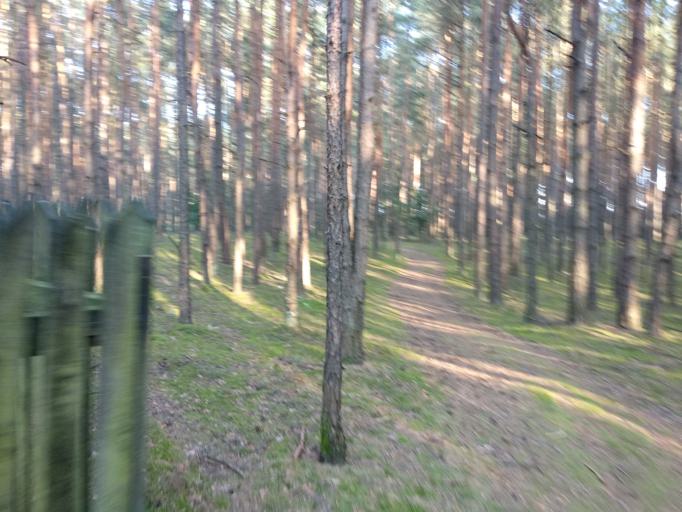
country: PL
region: Masovian Voivodeship
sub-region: Powiat pultuski
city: Obryte
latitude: 52.7522
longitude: 21.1997
